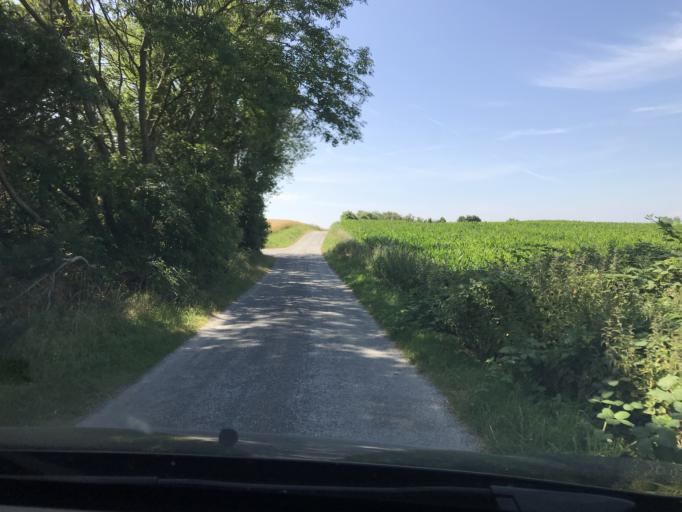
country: DK
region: South Denmark
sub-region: AEro Kommune
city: AEroskobing
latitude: 54.9007
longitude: 10.3192
